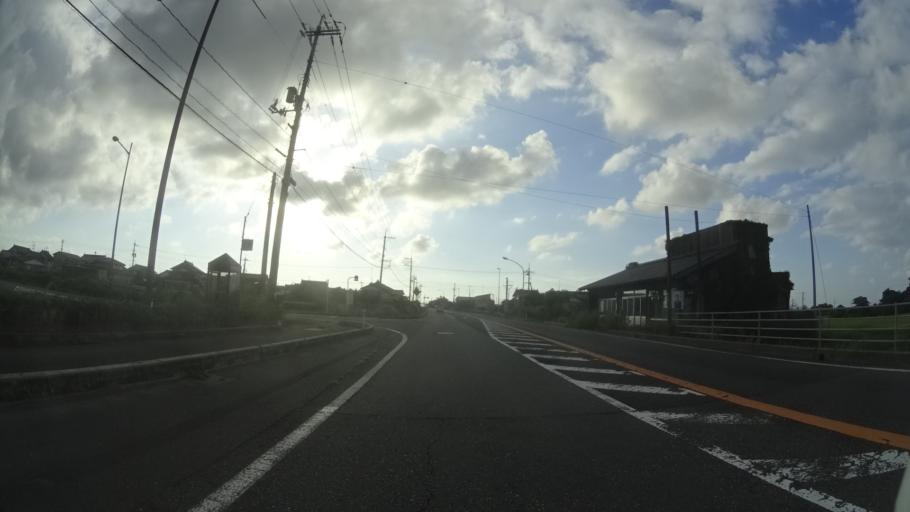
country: JP
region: Tottori
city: Kurayoshi
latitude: 35.5234
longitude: 133.5934
